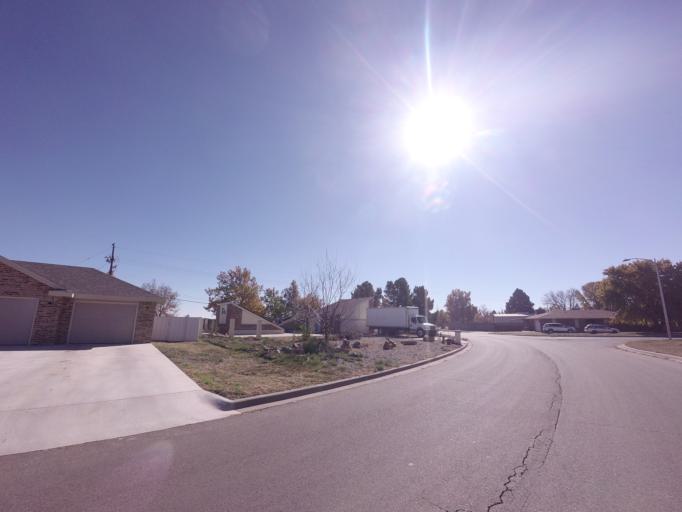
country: US
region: New Mexico
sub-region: Curry County
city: Clovis
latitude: 34.4223
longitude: -103.1883
